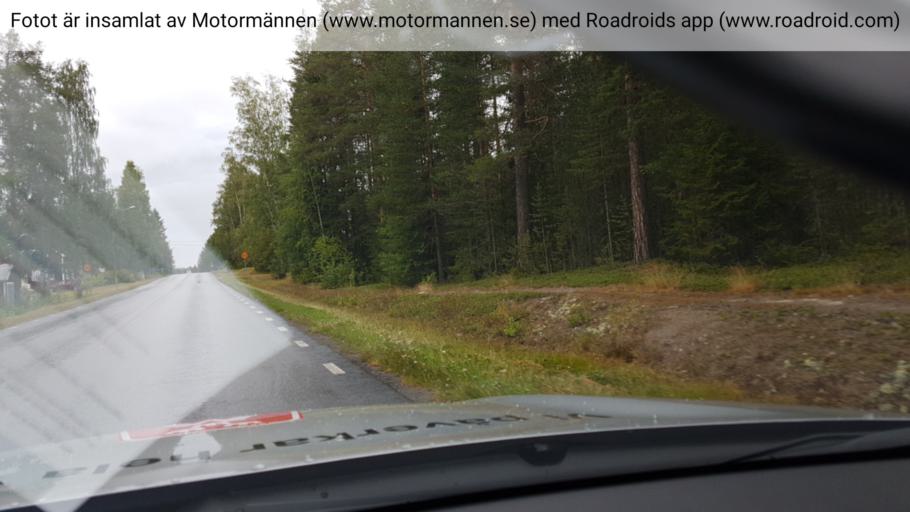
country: SE
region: Norrbotten
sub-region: Alvsbyns Kommun
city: AElvsbyn
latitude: 66.0933
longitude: 20.9452
